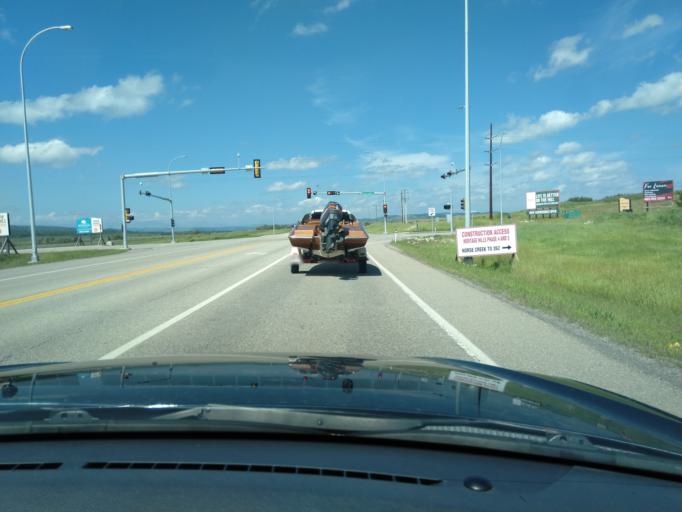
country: CA
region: Alberta
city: Cochrane
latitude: 51.2061
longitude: -114.5117
